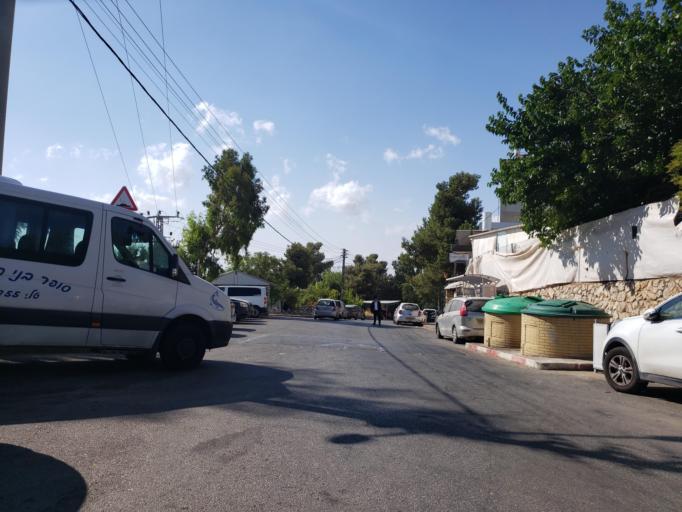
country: IL
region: Northern District
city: Safed
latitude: 32.9581
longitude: 35.5003
